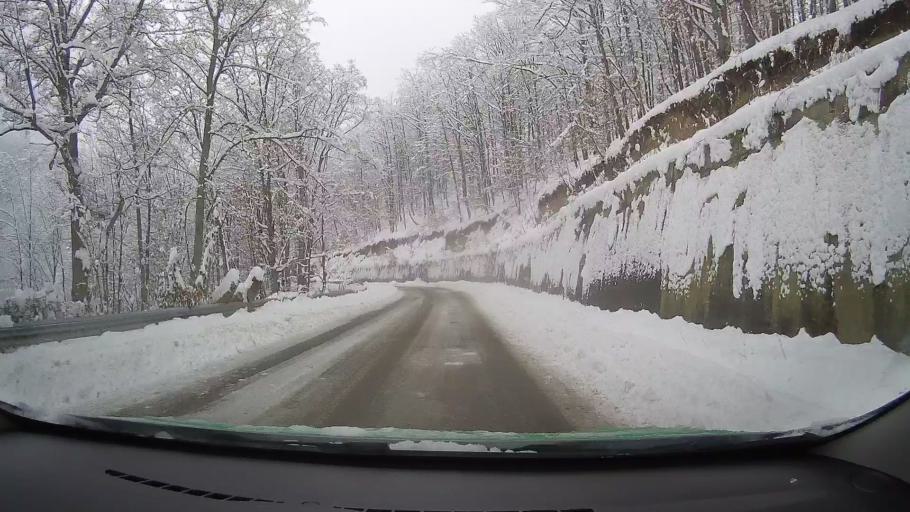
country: RO
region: Alba
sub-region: Comuna Sugag
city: Dobra
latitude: 45.7634
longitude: 23.6628
